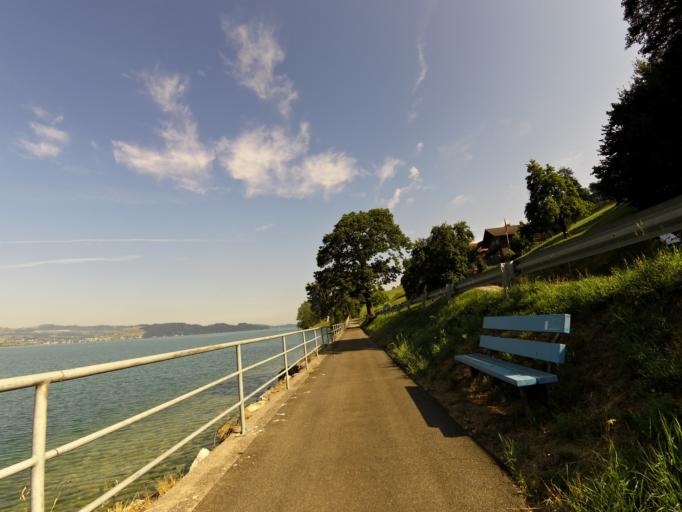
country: CH
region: Schwyz
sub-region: Bezirk Schwyz
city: Arth
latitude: 47.0745
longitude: 8.5276
